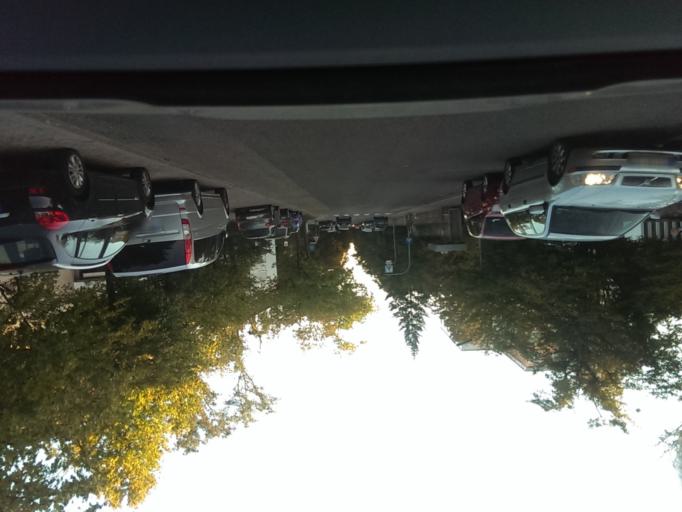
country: DE
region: Baden-Wuerttemberg
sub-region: Karlsruhe Region
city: Karlsruhe
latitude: 49.0151
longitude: 8.4224
